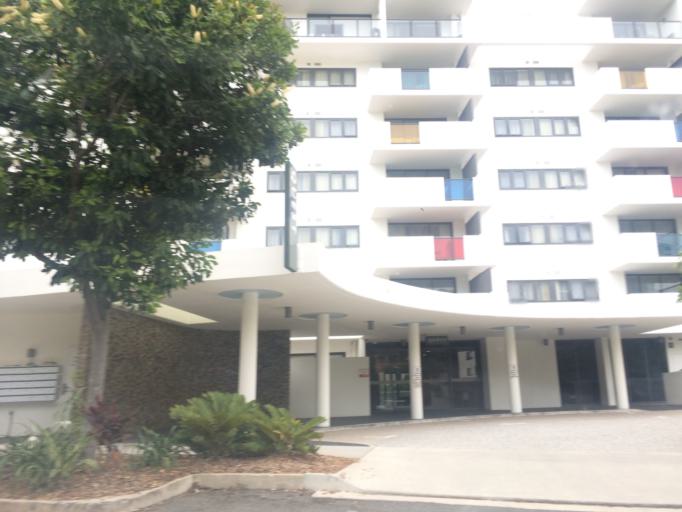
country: AU
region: Queensland
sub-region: Brisbane
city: Spring Hill
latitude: -27.4551
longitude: 153.0149
